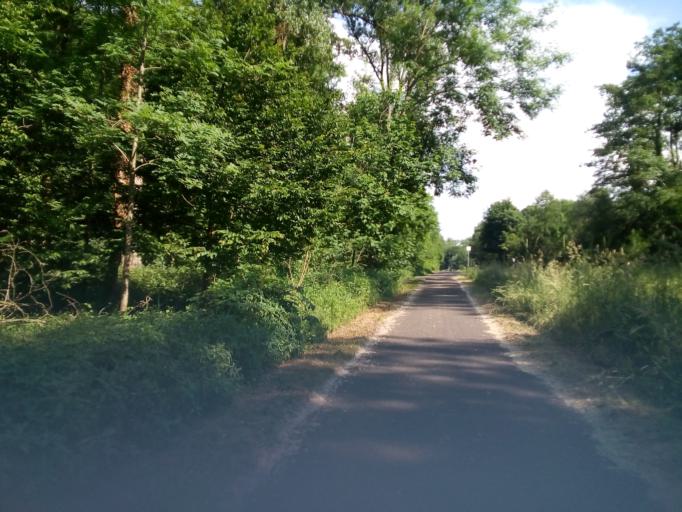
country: DE
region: Baden-Wuerttemberg
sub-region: Karlsruhe Region
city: Lichtenau
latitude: 48.7276
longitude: 7.9895
